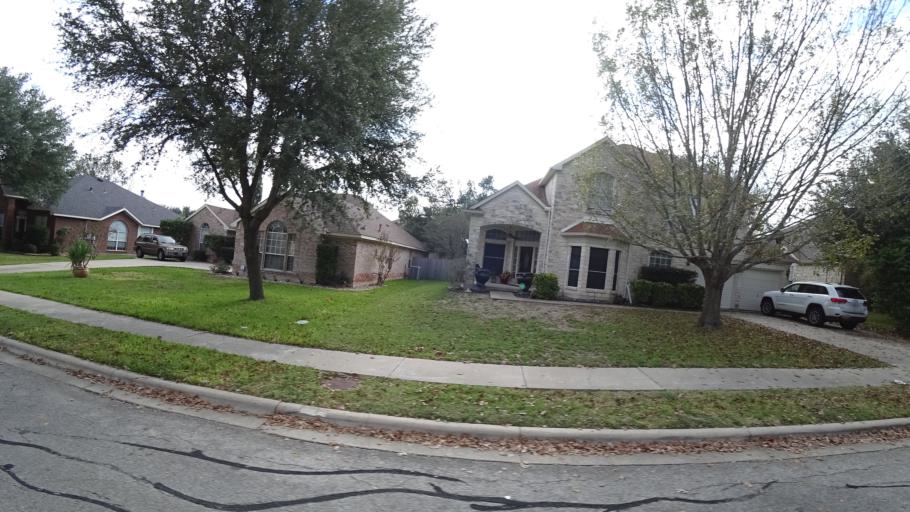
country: US
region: Texas
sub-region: Travis County
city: Pflugerville
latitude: 30.4308
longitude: -97.6258
